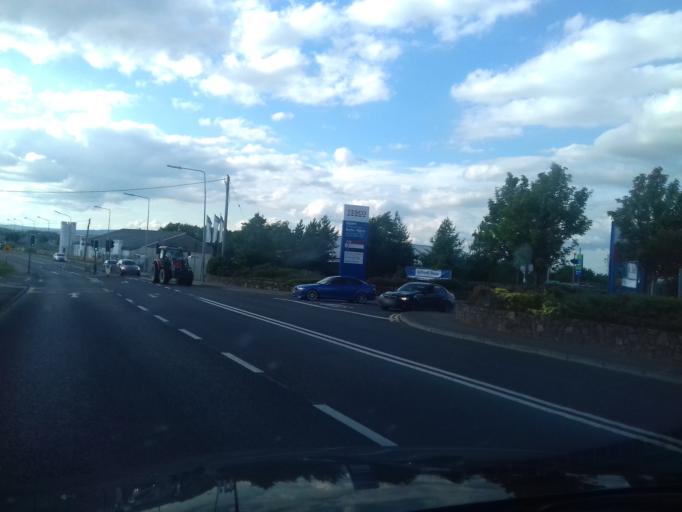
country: IE
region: Leinster
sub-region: Loch Garman
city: New Ross
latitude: 52.3902
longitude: -6.9302
